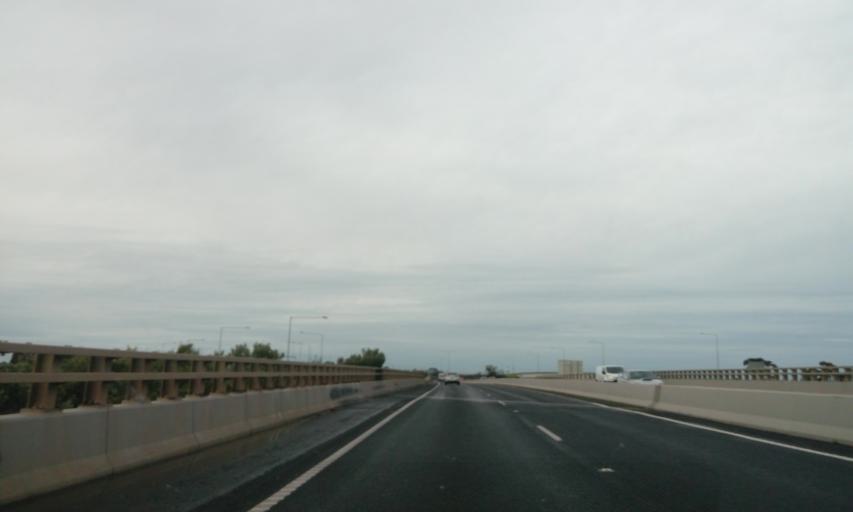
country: AU
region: Victoria
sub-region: Greater Geelong
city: Lara
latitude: -38.0574
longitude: 144.3861
